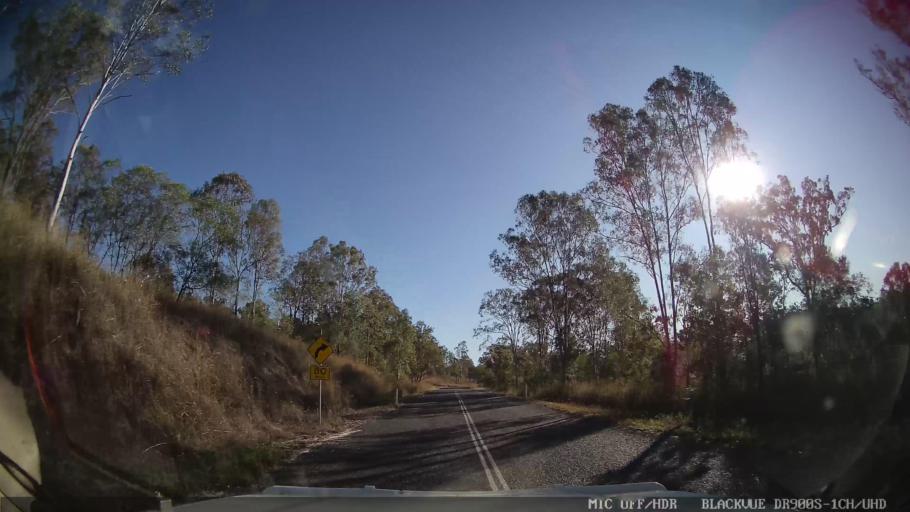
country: AU
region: Queensland
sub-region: Bundaberg
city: Sharon
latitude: -24.8052
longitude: 151.6566
